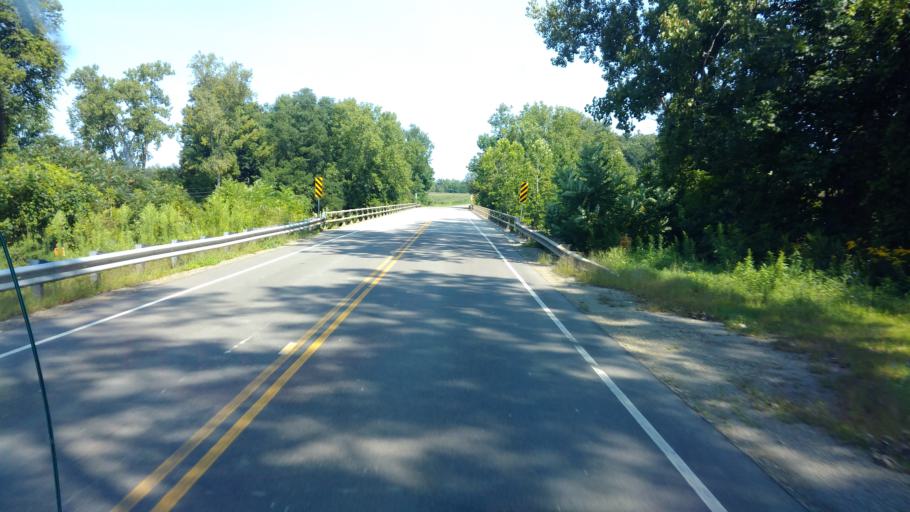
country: US
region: New York
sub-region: Allegany County
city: Belmont
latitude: 42.2632
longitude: -78.0521
